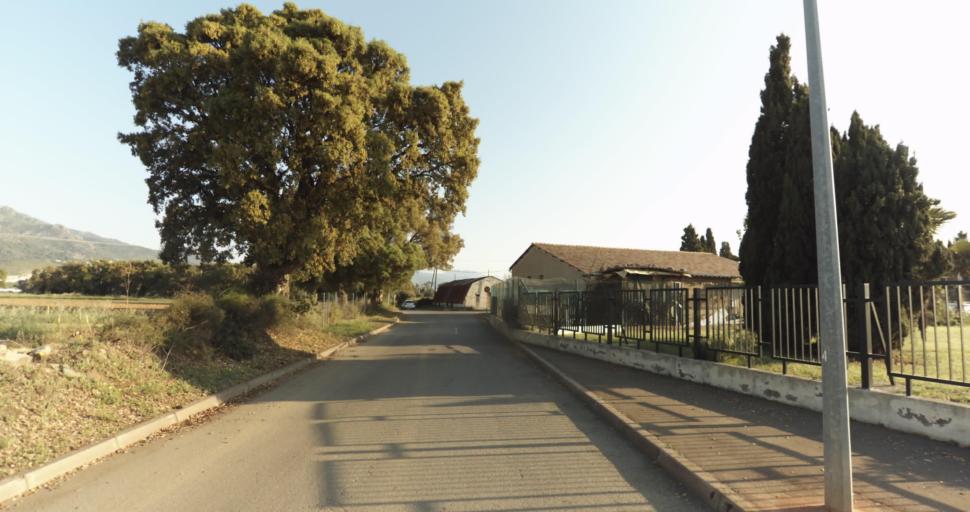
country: FR
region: Corsica
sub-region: Departement de la Haute-Corse
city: Biguglia
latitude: 42.6087
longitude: 9.4439
